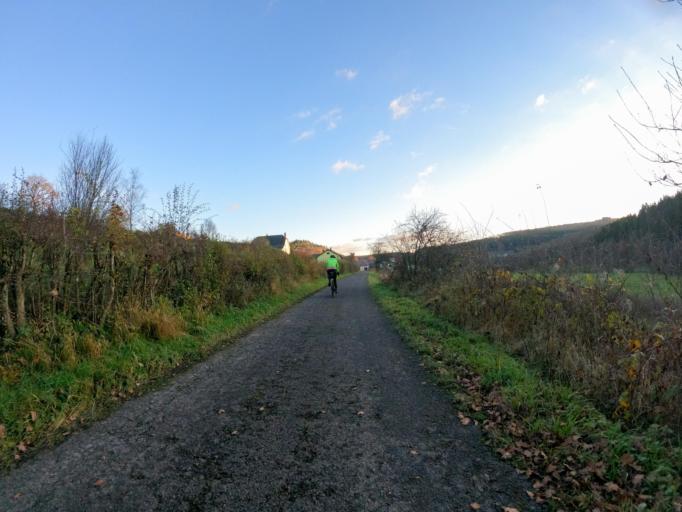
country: LU
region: Diekirch
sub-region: Canton de Wiltz
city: Bavigne
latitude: 49.9271
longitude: 5.8454
